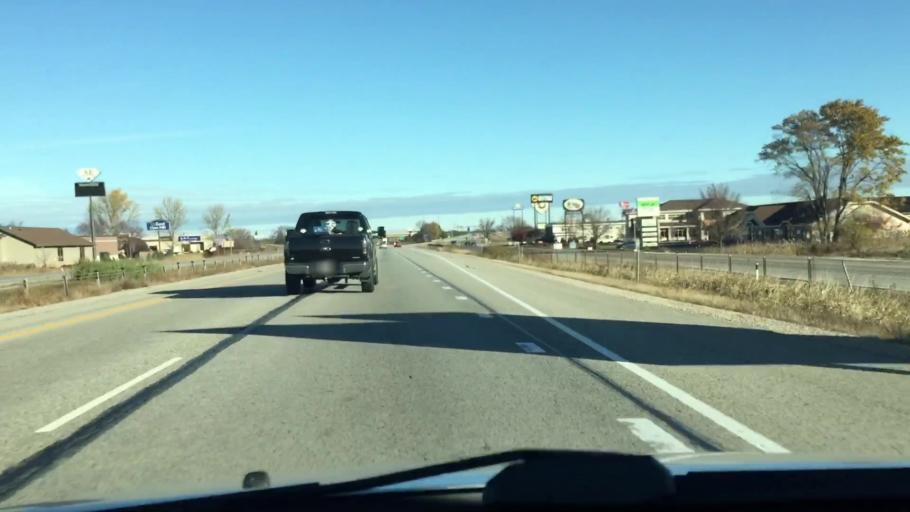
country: US
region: Wisconsin
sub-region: Fond du Lac County
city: North Fond du Lac
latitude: 43.7788
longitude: -88.4823
